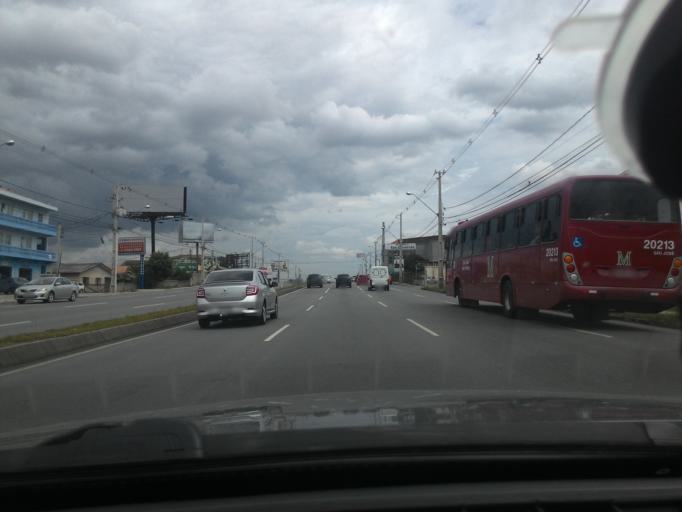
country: BR
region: Parana
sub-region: Sao Jose Dos Pinhais
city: Sao Jose dos Pinhais
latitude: -25.5221
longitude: -49.1986
